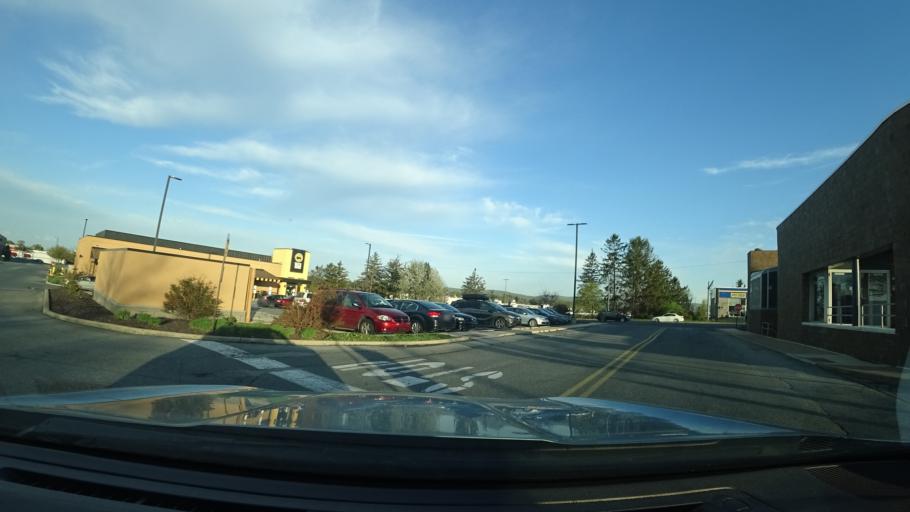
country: US
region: Pennsylvania
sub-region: Lehigh County
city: Fullerton
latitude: 40.6335
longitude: -75.4833
